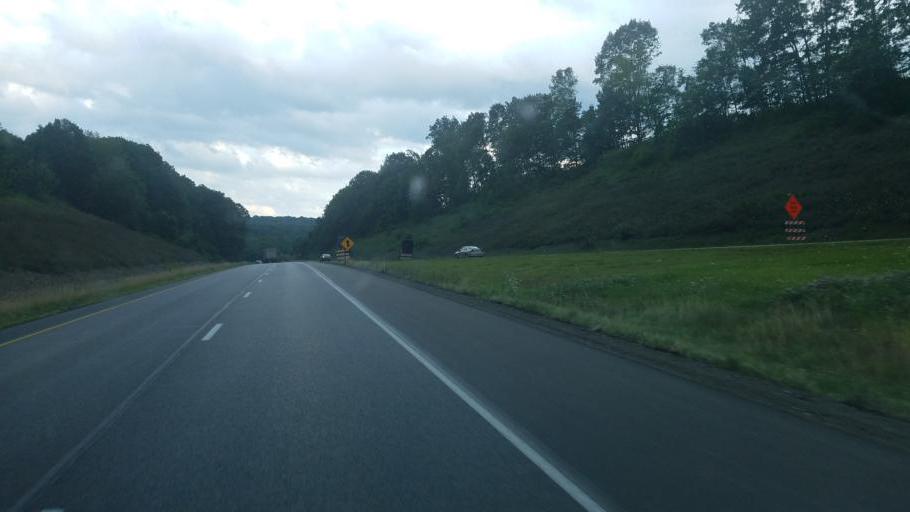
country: US
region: Pennsylvania
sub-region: Butler County
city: Zelienople
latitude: 40.7569
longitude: -80.1145
